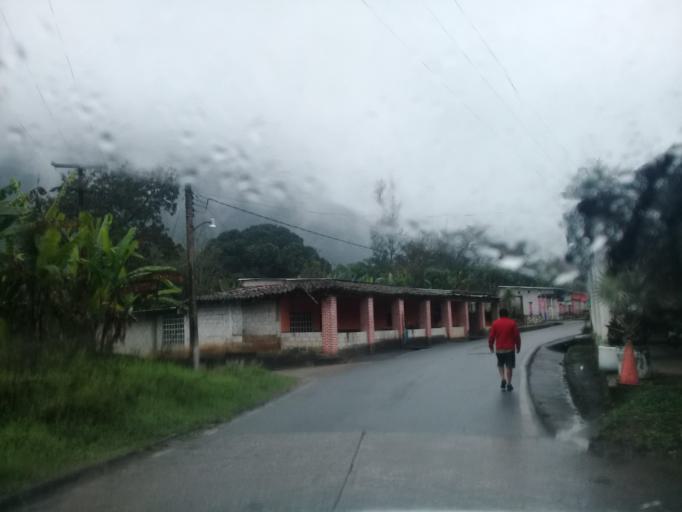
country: MX
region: Veracruz
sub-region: Amatlan de los Reyes
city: Centro de Readaptacion Social
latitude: 18.8021
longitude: -96.9504
